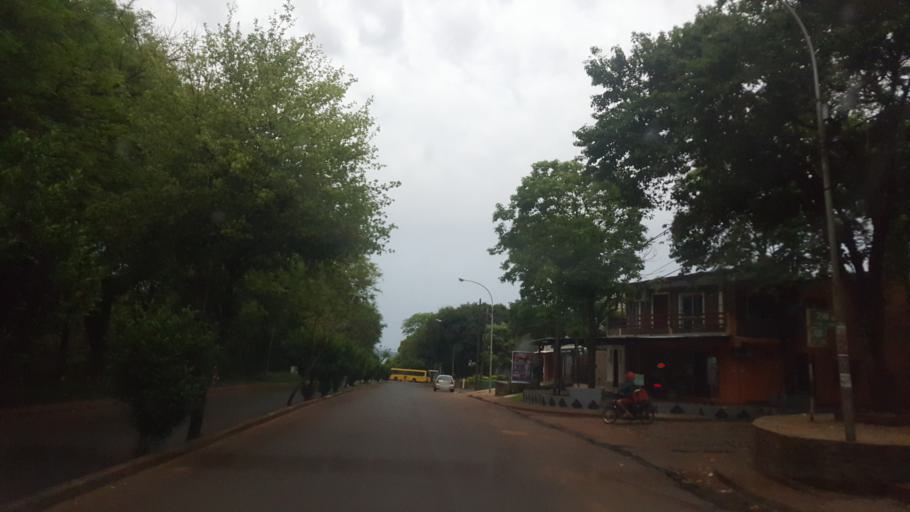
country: AR
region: Misiones
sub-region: Departamento de Capital
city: Posadas
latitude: -27.3580
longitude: -55.9380
